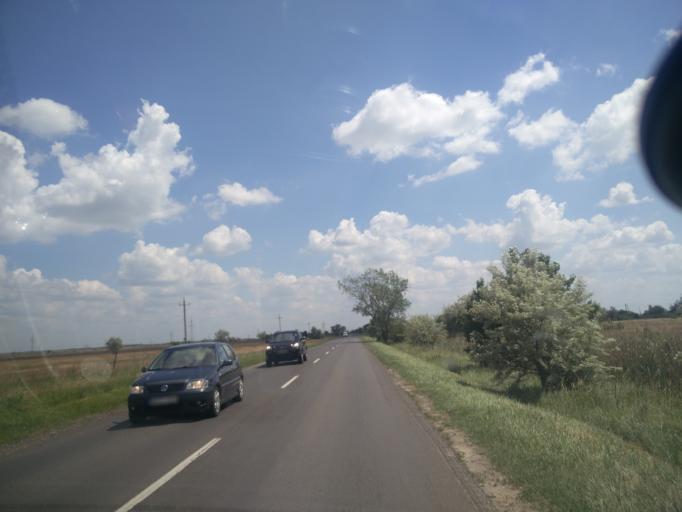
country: HU
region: Csongrad
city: Sandorfalva
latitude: 46.3456
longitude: 20.1289
